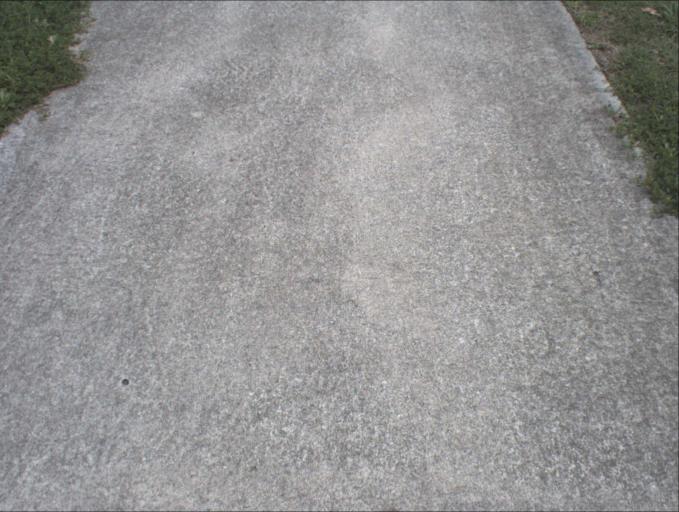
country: AU
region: Queensland
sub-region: Logan
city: Cedar Vale
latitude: -27.8305
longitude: 153.0239
